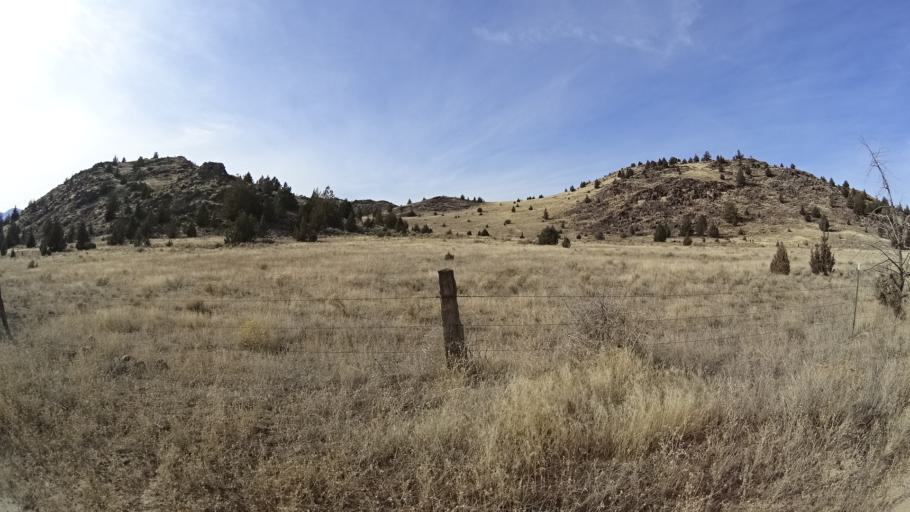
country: US
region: California
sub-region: Siskiyou County
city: Weed
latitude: 41.5677
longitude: -122.4686
